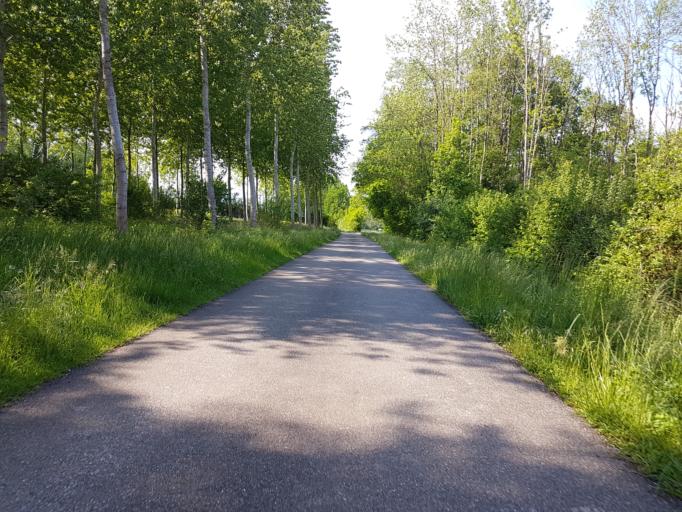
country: FR
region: Rhone-Alpes
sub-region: Departement de l'Ain
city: Culoz
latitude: 45.8816
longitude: 5.8342
